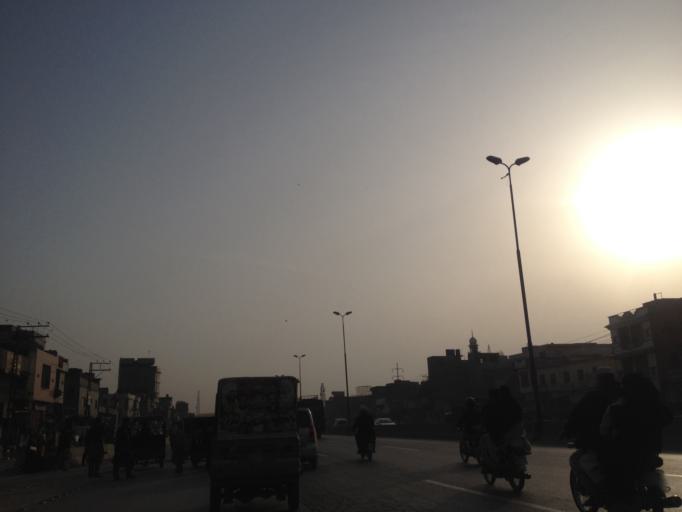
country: PK
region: Punjab
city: Lahore
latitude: 31.5652
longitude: 74.2811
